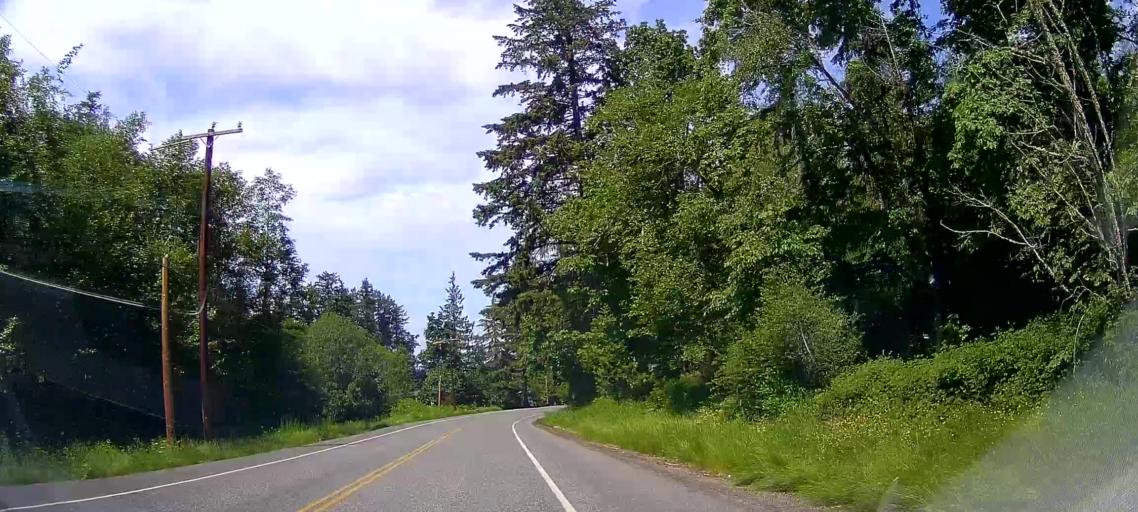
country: US
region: Washington
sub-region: Skagit County
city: Mount Vernon
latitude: 48.4041
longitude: -122.3058
